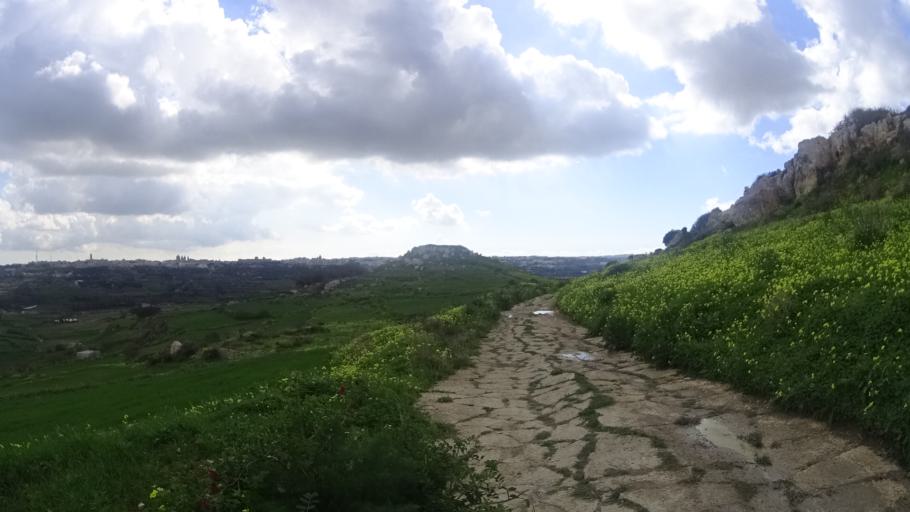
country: MT
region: L-Imtarfa
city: Imtarfa
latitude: 35.9018
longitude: 14.3841
